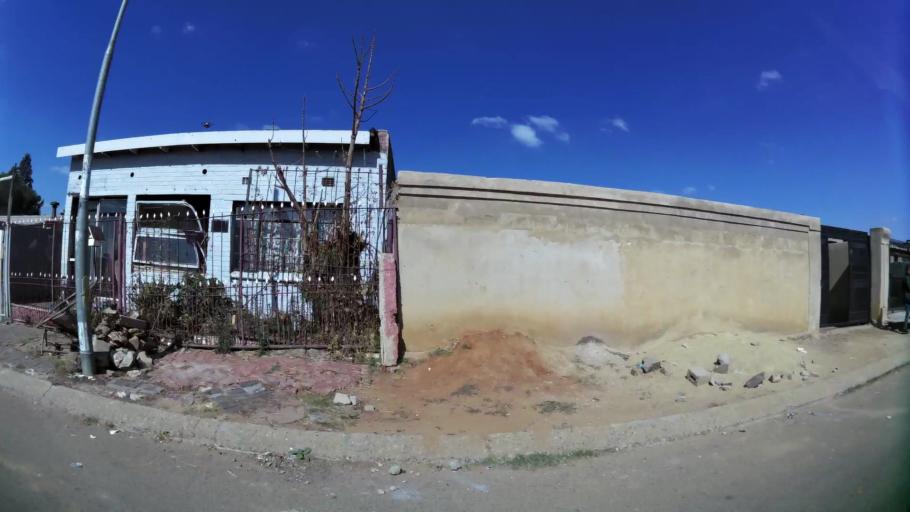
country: ZA
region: Gauteng
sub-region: City of Johannesburg Metropolitan Municipality
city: Soweto
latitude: -26.2494
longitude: 27.8863
